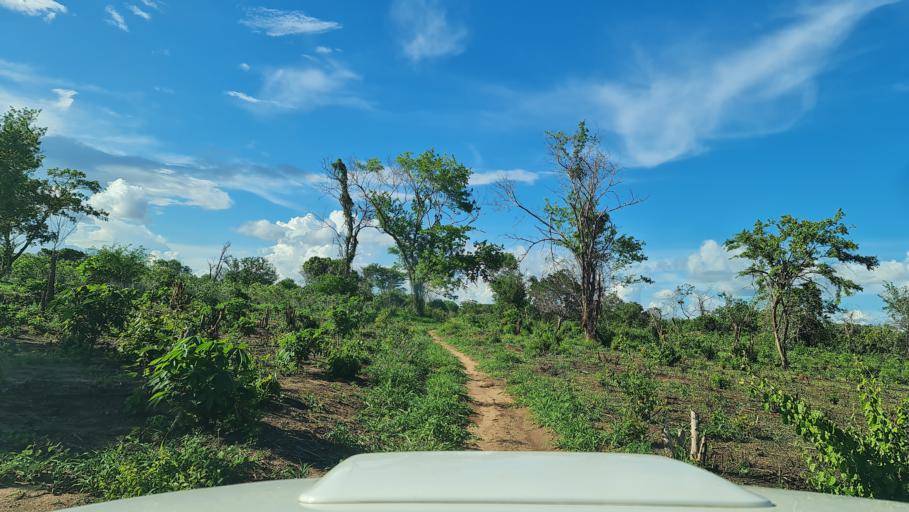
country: MZ
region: Nampula
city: Ilha de Mocambique
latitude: -15.2668
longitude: 40.1864
